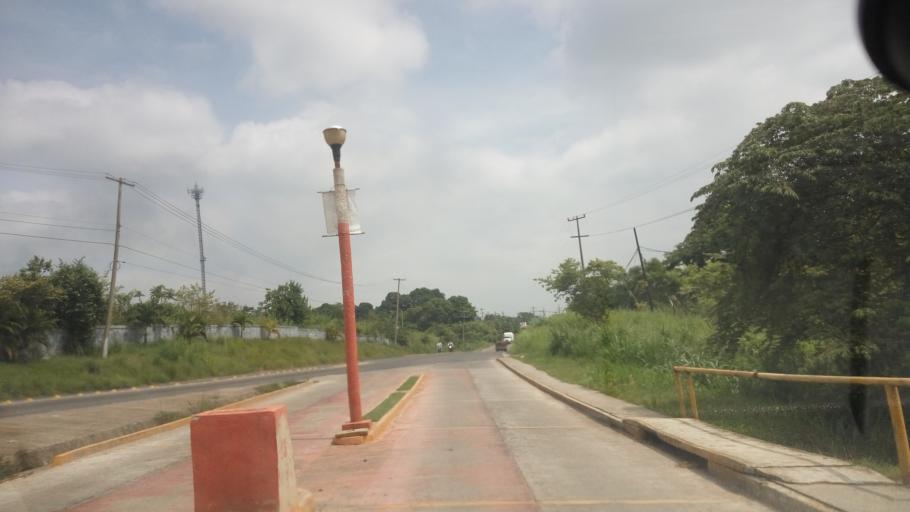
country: MX
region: Chiapas
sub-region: Reforma
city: El Carmen (El Limon)
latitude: 17.8748
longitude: -93.1510
